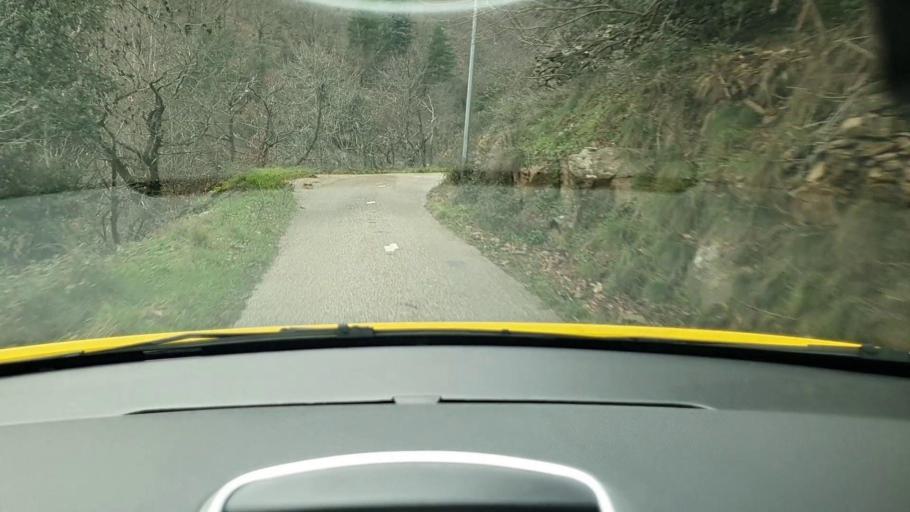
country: FR
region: Languedoc-Roussillon
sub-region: Departement du Gard
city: Besseges
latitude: 44.3745
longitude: 4.0383
